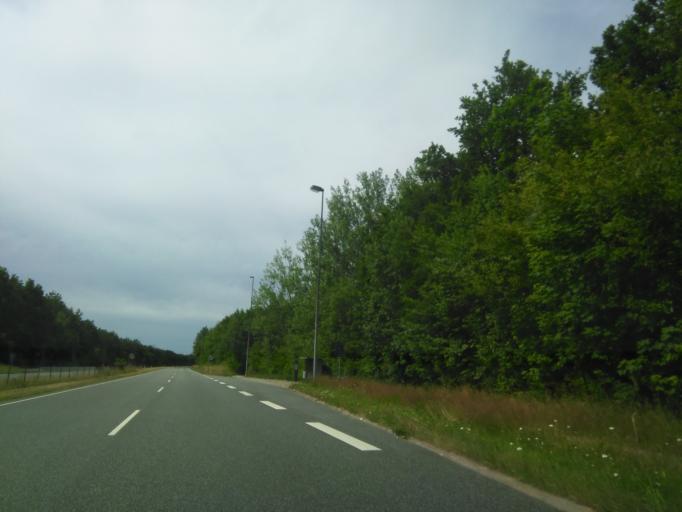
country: DK
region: Central Jutland
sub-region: Arhus Kommune
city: Tranbjerg
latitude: 56.0917
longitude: 10.1329
